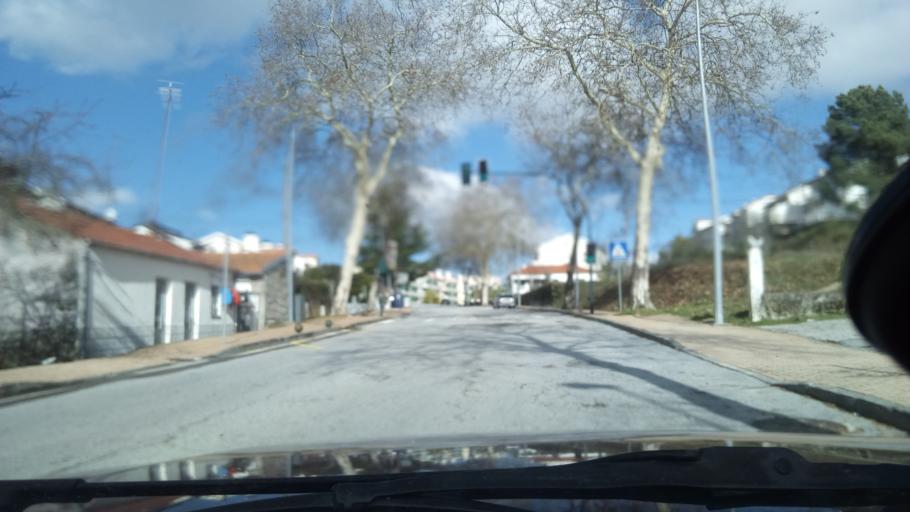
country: PT
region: Guarda
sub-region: Guarda
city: Guarda
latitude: 40.5378
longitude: -7.2847
